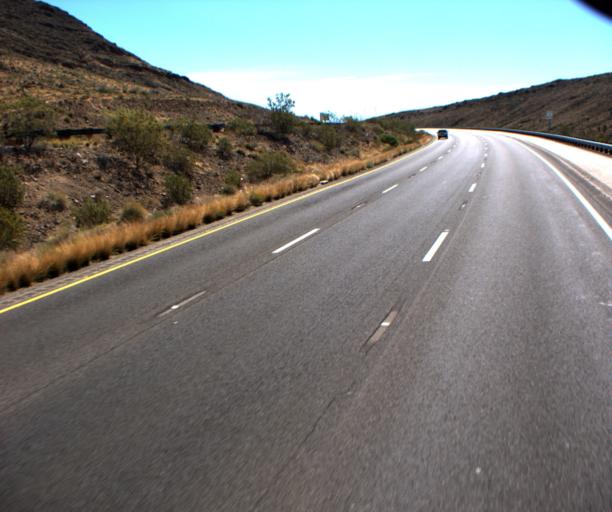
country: US
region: Arizona
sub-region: Mohave County
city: Kingman
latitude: 35.2134
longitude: -114.1137
